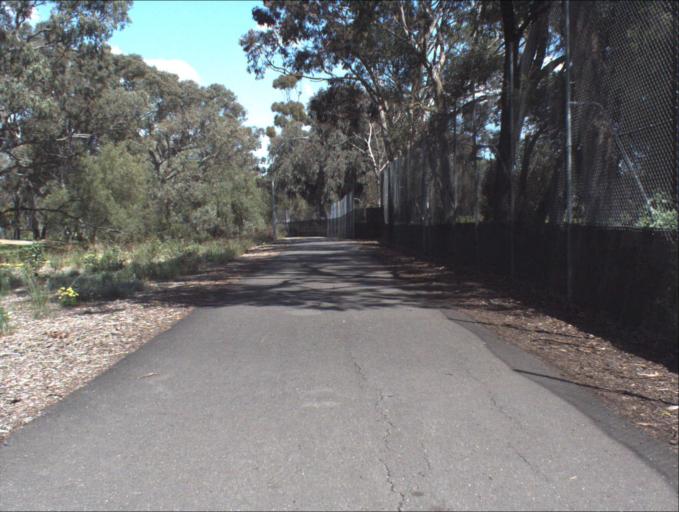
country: AU
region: South Australia
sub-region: Port Adelaide Enfield
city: Gilles Plains
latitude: -34.8440
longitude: 138.6655
